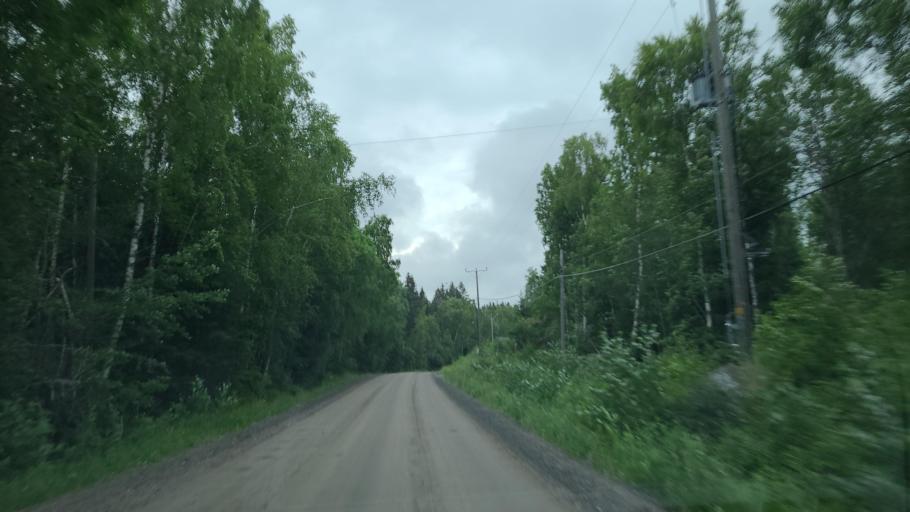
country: FI
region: Ostrobothnia
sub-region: Vaasa
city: Replot
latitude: 63.3050
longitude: 21.1540
